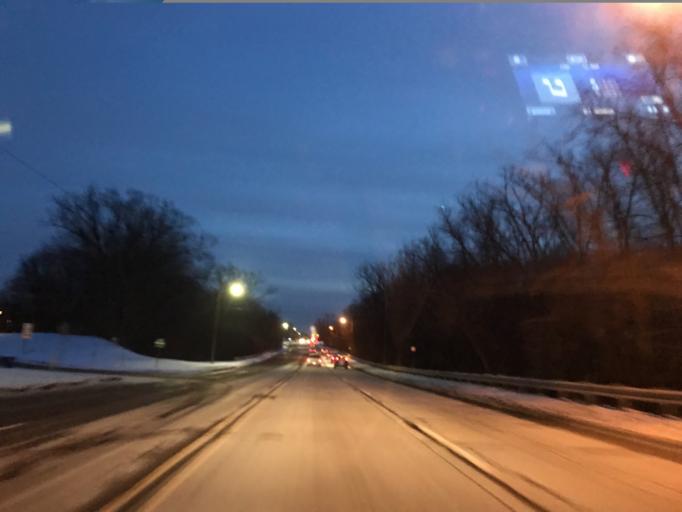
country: US
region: Michigan
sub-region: Wayne County
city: Redford
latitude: 42.4070
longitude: -83.3154
